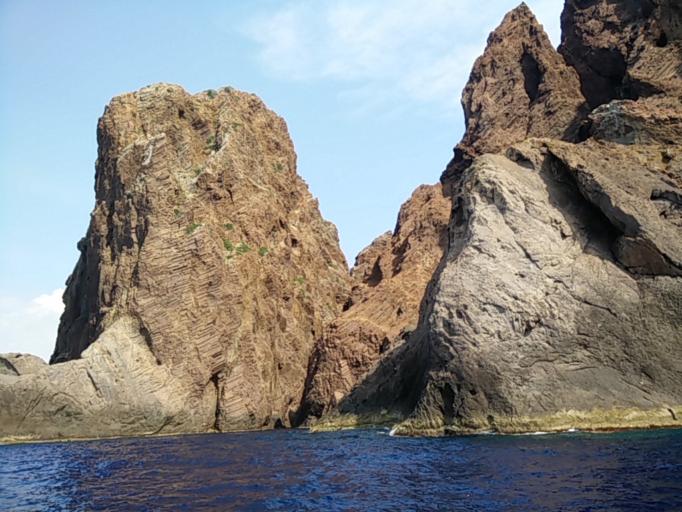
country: FR
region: Corsica
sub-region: Departement de la Corse-du-Sud
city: Cargese
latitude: 42.3787
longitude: 8.5461
